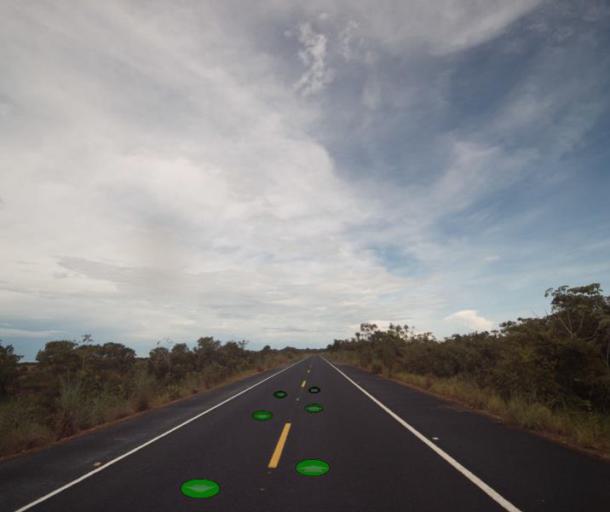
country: BR
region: Goias
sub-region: Sao Miguel Do Araguaia
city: Sao Miguel do Araguaia
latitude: -13.2385
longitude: -50.5474
